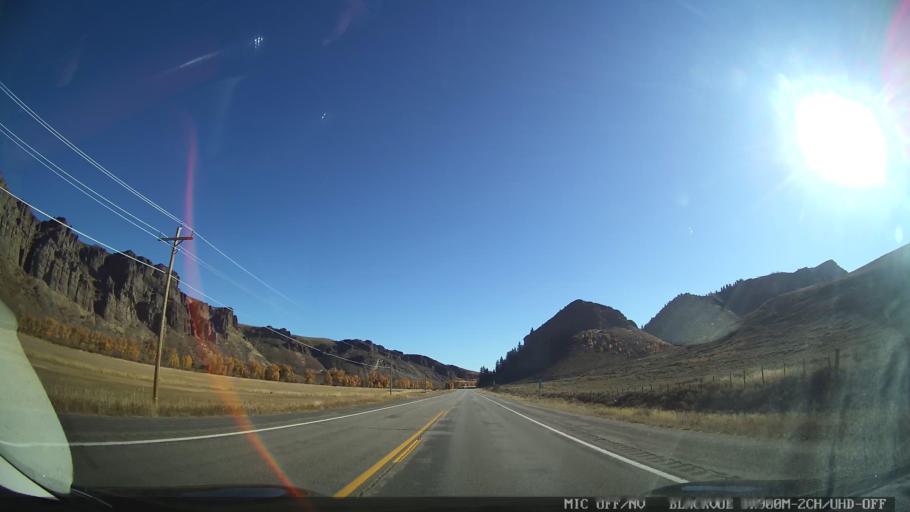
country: US
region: Colorado
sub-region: Grand County
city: Hot Sulphur Springs
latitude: 40.0816
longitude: -106.0862
